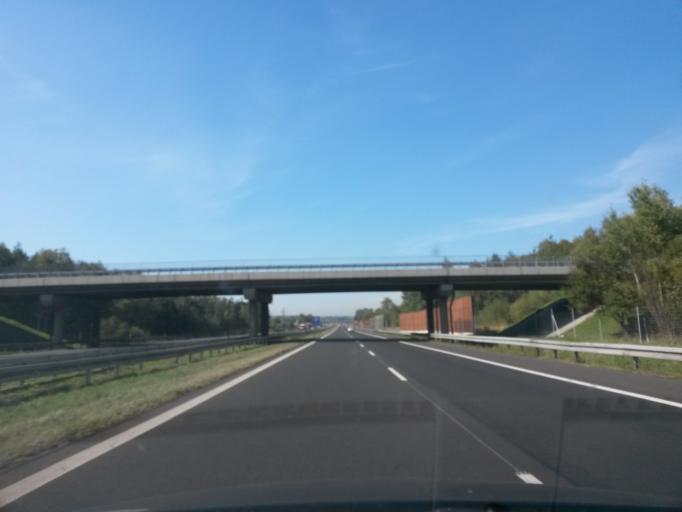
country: PL
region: Lesser Poland Voivodeship
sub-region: Powiat chrzanowski
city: Trzebinia
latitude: 50.1434
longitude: 19.4457
